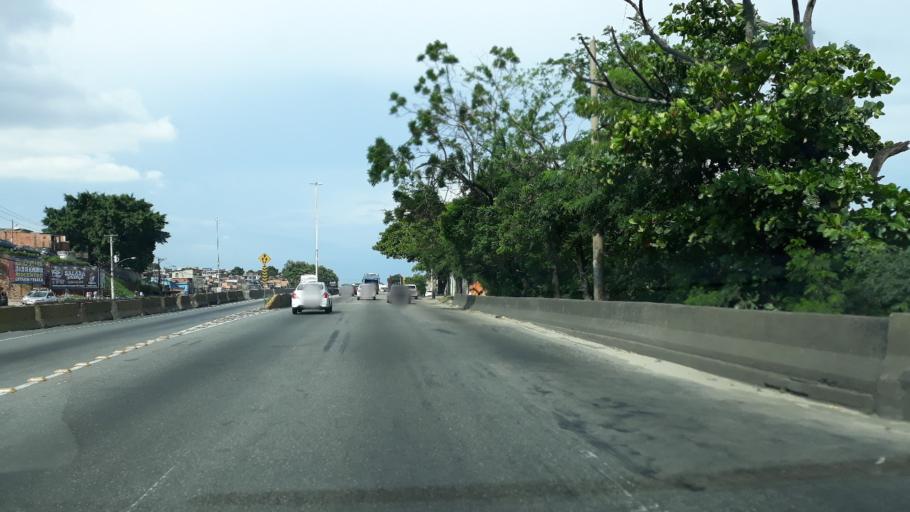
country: BR
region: Rio de Janeiro
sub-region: Sao Joao De Meriti
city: Sao Joao de Meriti
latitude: -22.8380
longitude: -43.3656
